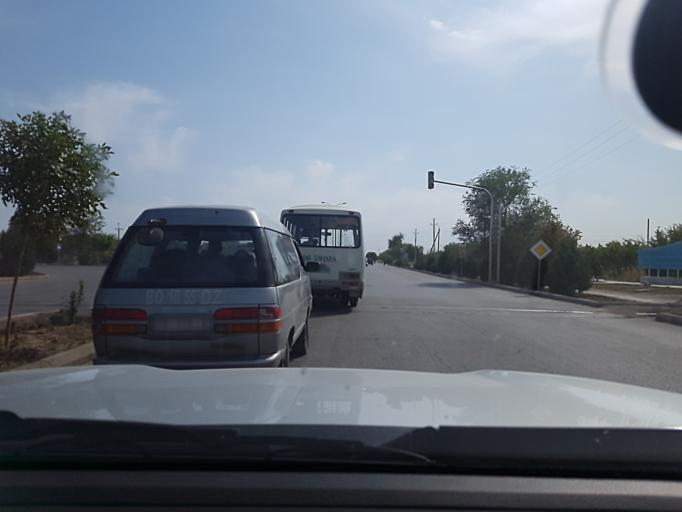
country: TM
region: Dasoguz
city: Dasoguz
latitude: 41.8565
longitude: 59.9417
